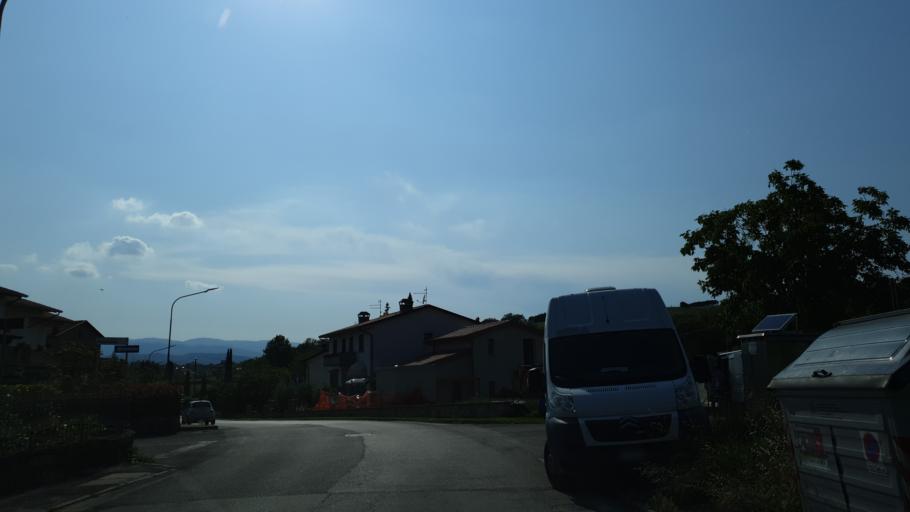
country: IT
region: Tuscany
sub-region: Province of Arezzo
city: Soci
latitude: 43.7400
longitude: 11.8131
